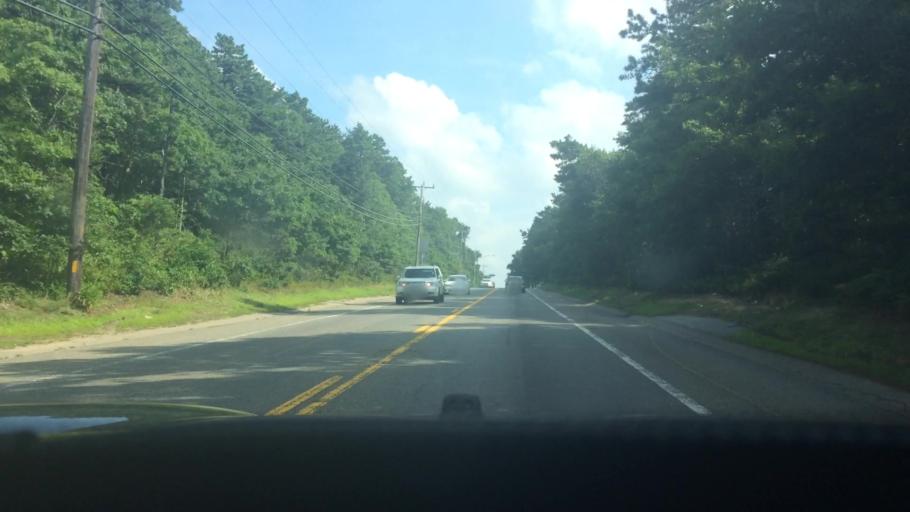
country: US
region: Massachusetts
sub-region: Barnstable County
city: Sandwich
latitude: 41.7359
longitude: -70.4920
